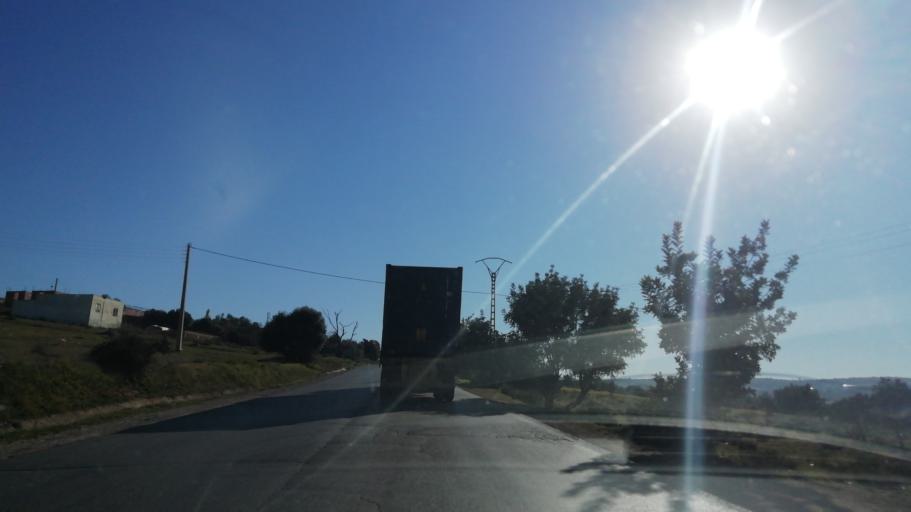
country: DZ
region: Relizane
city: Smala
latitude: 35.6790
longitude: 0.8001
